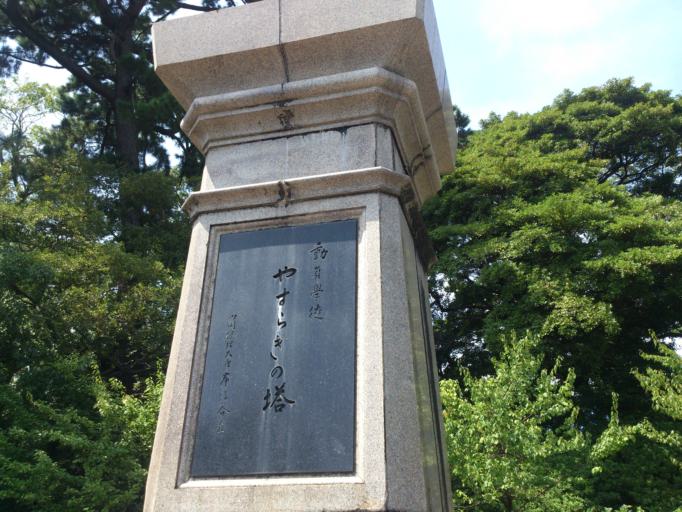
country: JP
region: Shizuoka
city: Shizuoka-shi
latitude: 34.9793
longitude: 138.3816
